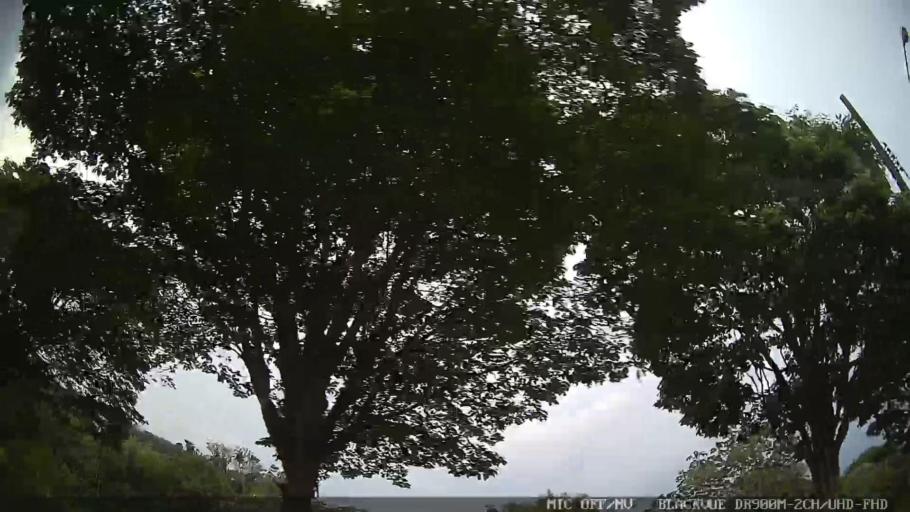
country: BR
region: Sao Paulo
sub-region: Braganca Paulista
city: Braganca Paulista
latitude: -22.9616
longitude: -46.5469
